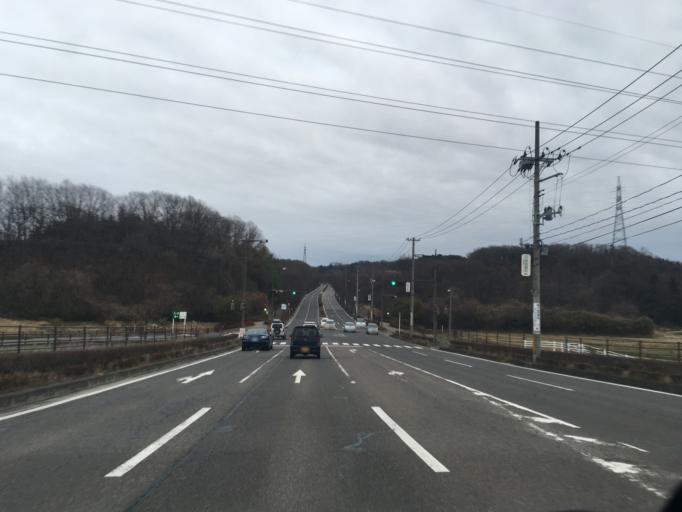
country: JP
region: Fukushima
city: Koriyama
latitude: 37.3943
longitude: 140.4124
